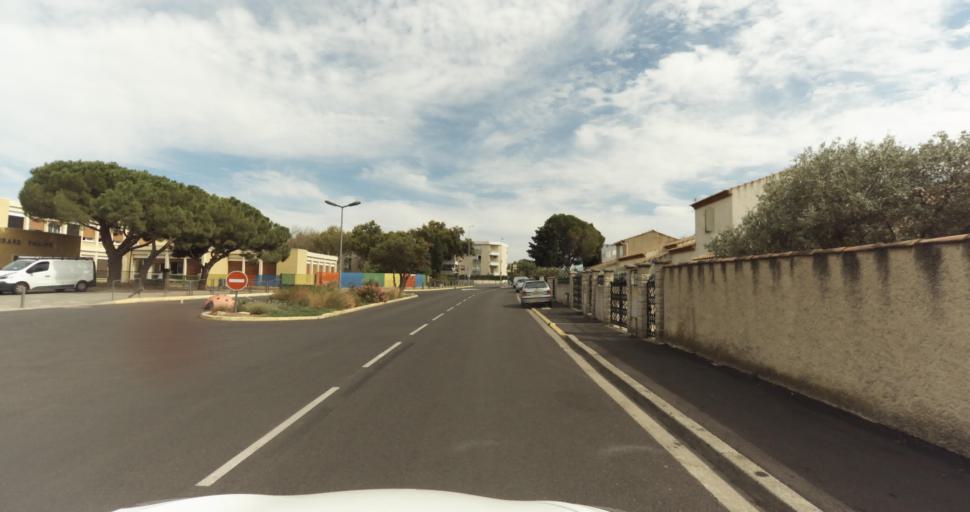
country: FR
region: Provence-Alpes-Cote d'Azur
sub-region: Departement des Bouches-du-Rhone
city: Miramas
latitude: 43.5771
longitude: 4.9960
